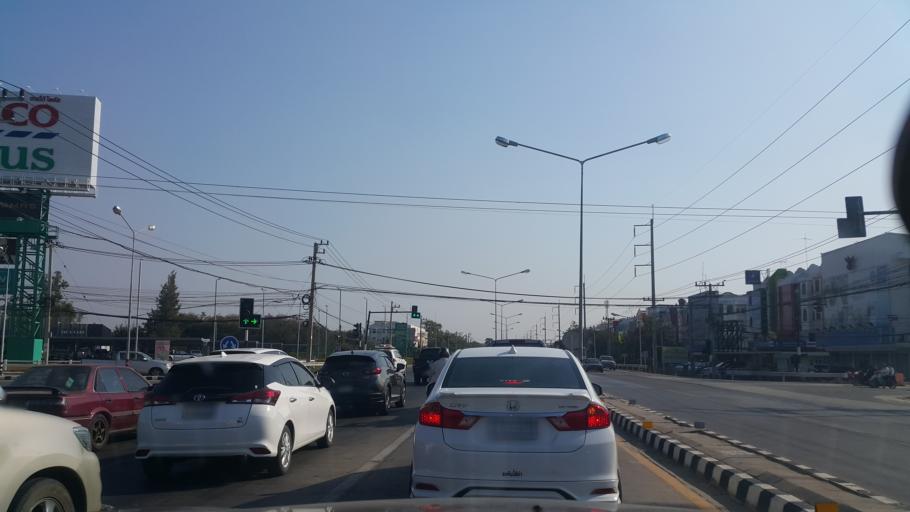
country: TH
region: Nakhon Ratchasima
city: Phimai
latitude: 15.2156
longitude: 102.4856
